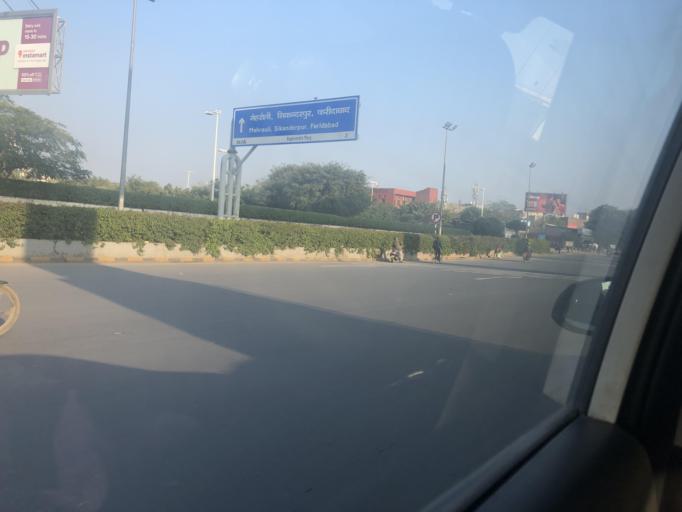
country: IN
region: Haryana
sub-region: Gurgaon
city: Gurgaon
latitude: 28.4873
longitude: 77.0936
